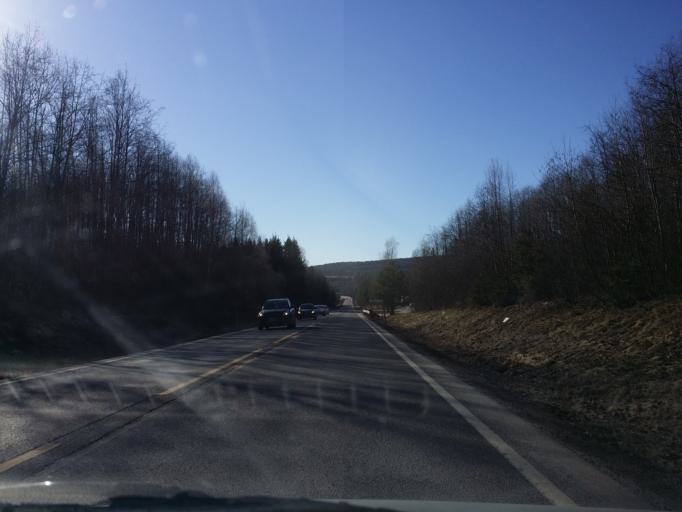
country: NO
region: Buskerud
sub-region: Ringerike
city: Honefoss
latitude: 60.1977
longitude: 10.2525
